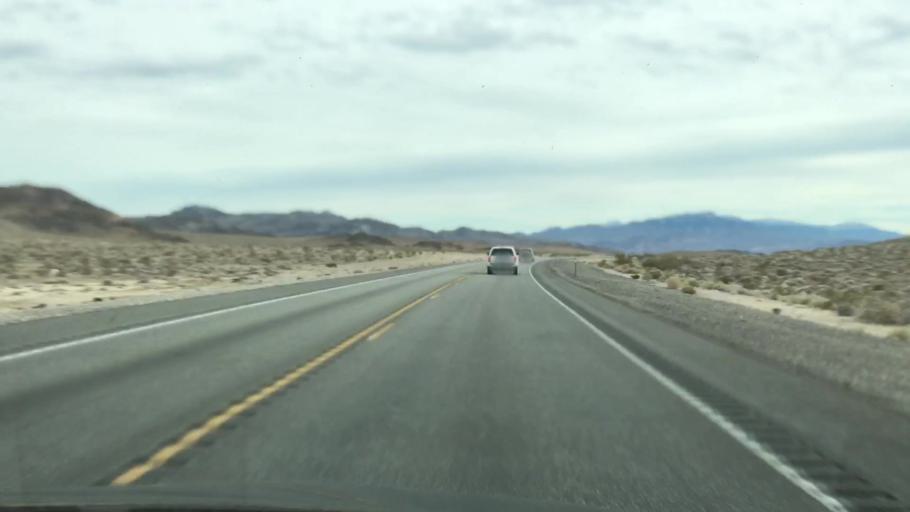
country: US
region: Nevada
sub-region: Nye County
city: Pahrump
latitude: 36.6238
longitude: -116.3008
